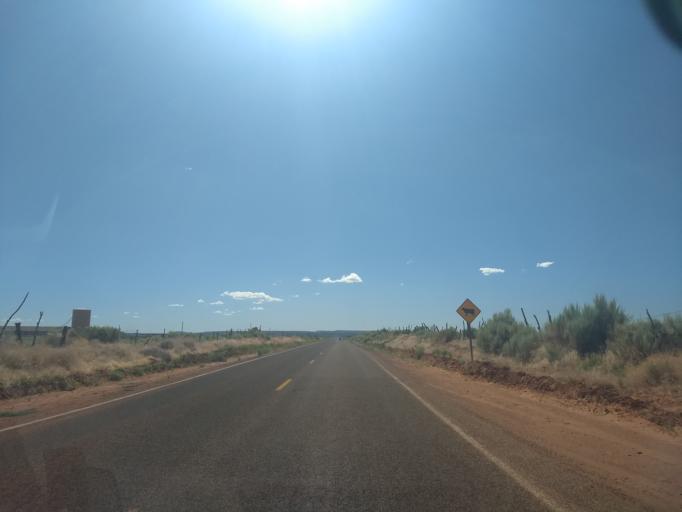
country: US
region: Arizona
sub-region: Mohave County
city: Colorado City
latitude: 36.9469
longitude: -112.9339
